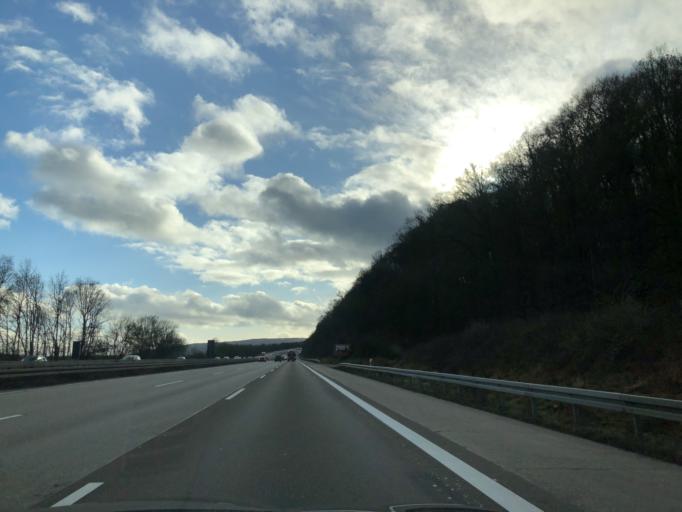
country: DE
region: Hesse
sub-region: Regierungsbezirk Darmstadt
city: Idstein
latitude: 50.2290
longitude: 8.2494
